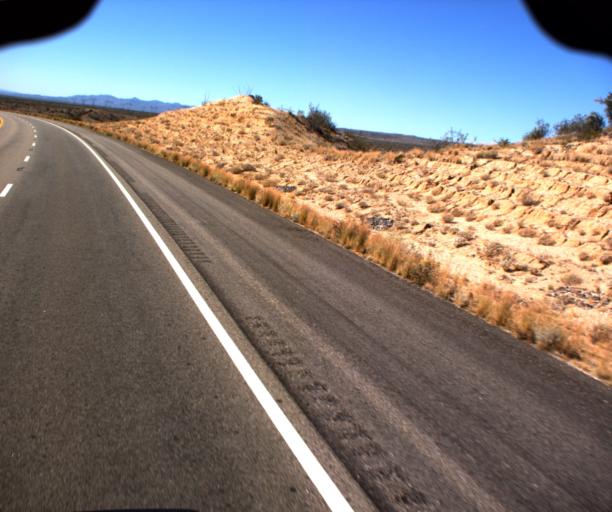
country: US
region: Arizona
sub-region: Mohave County
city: Kingman
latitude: 34.9037
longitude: -113.6573
